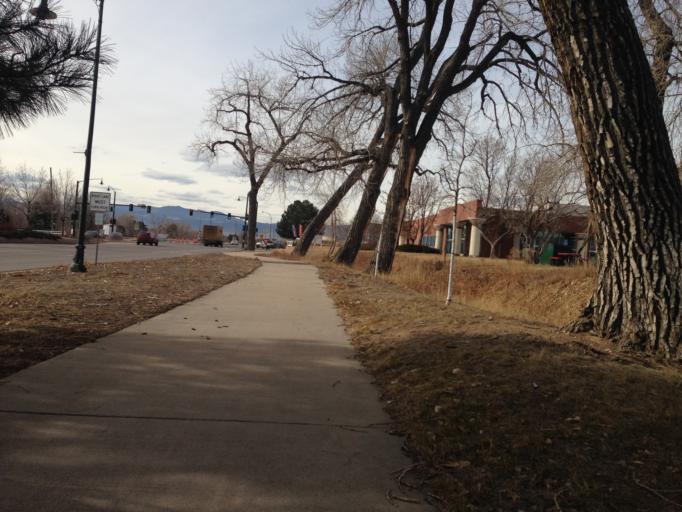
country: US
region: Colorado
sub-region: Adams County
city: Westminster
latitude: 39.8567
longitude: -105.0619
